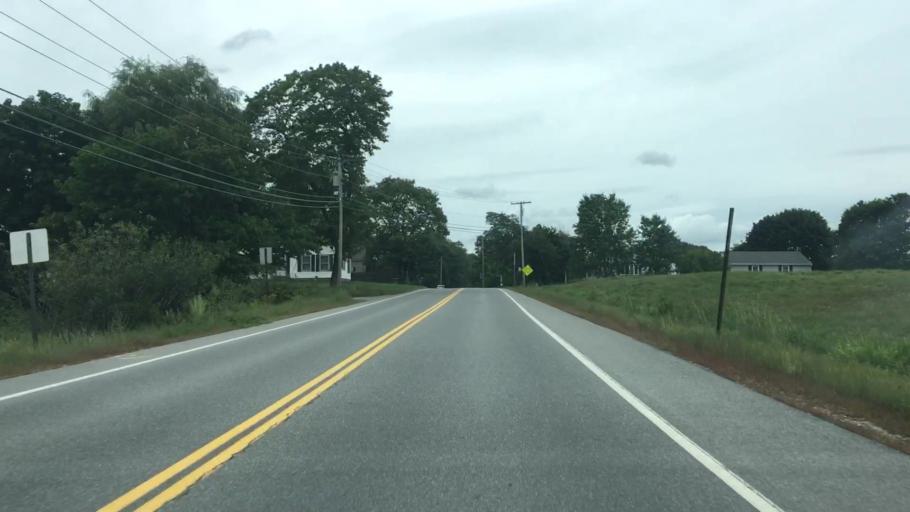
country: US
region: Maine
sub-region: Cumberland County
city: Yarmouth
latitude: 43.8280
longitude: -70.1955
